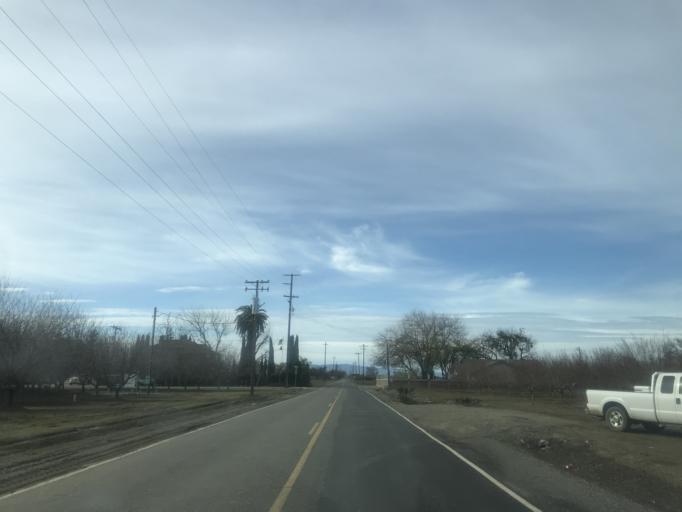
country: US
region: California
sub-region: Yolo County
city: Woodland
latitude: 38.6634
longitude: -121.8338
